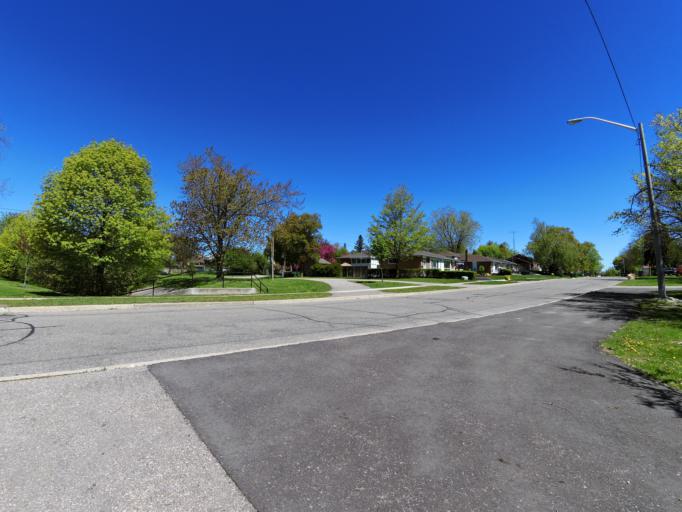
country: CA
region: Ontario
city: Brampton
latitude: 43.7107
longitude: -79.7057
